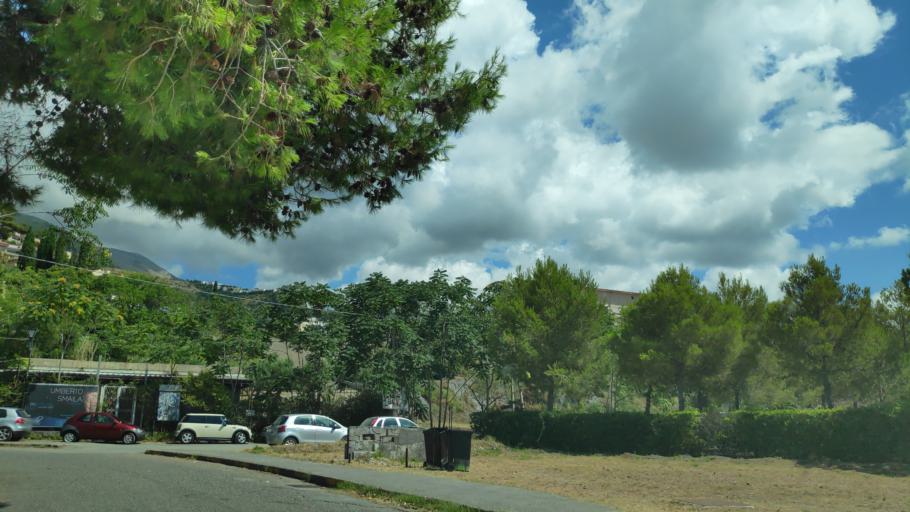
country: IT
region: Calabria
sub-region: Provincia di Cosenza
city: Praia a Mare
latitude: 39.8728
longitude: 15.7867
